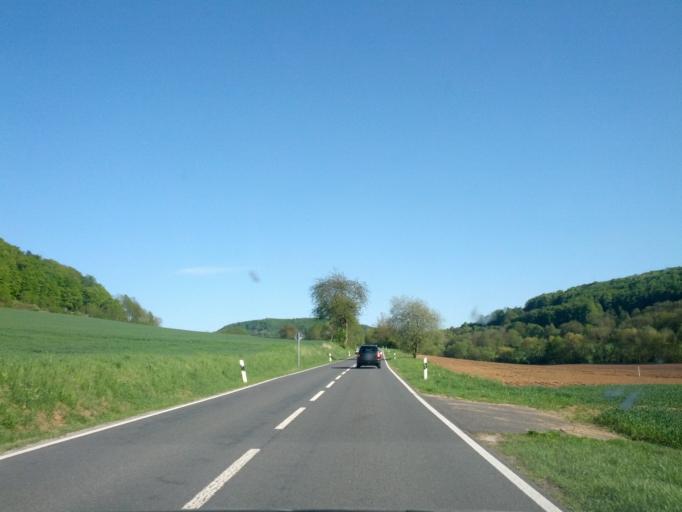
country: DE
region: Thuringia
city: Geismar
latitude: 51.2227
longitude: 10.1895
